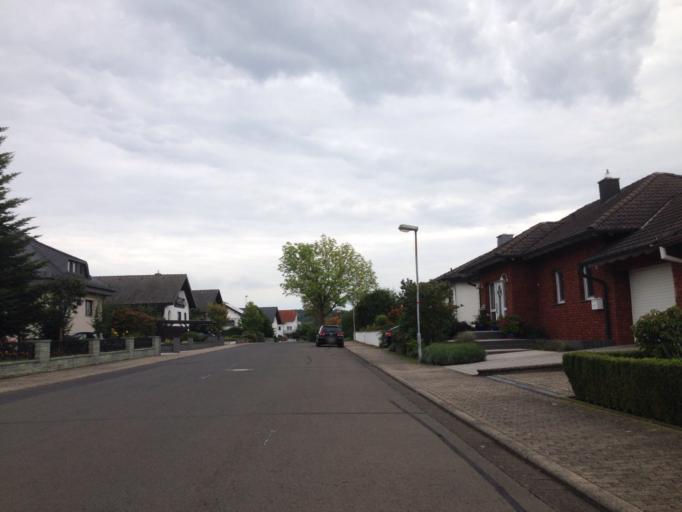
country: DE
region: Hesse
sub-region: Regierungsbezirk Giessen
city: Alten Buseck
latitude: 50.6240
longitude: 8.7581
